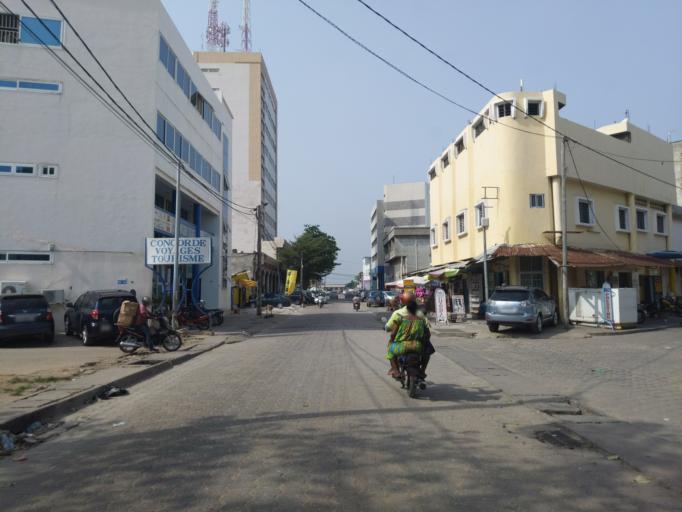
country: BJ
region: Littoral
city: Cotonou
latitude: 6.3558
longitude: 2.4397
